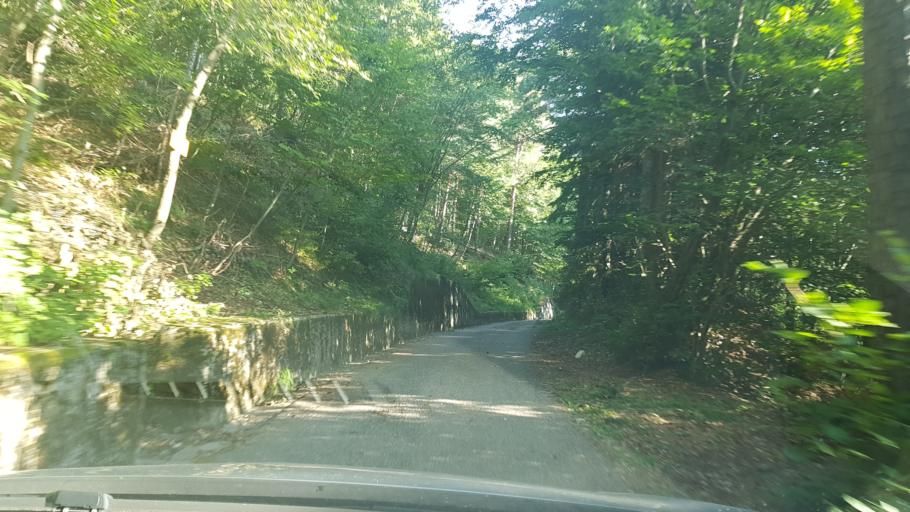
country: IT
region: Friuli Venezia Giulia
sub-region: Provincia di Udine
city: Moggio Udinese
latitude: 46.4400
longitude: 13.2117
